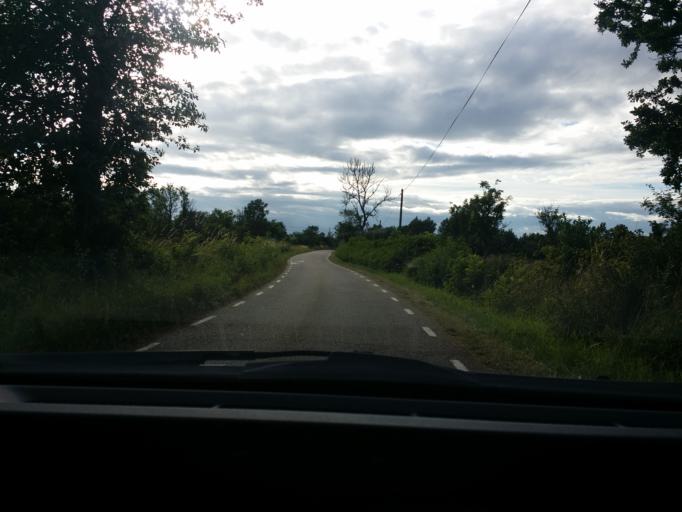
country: SE
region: Kalmar
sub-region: Borgholms Kommun
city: Borgholm
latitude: 57.1130
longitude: 16.9808
